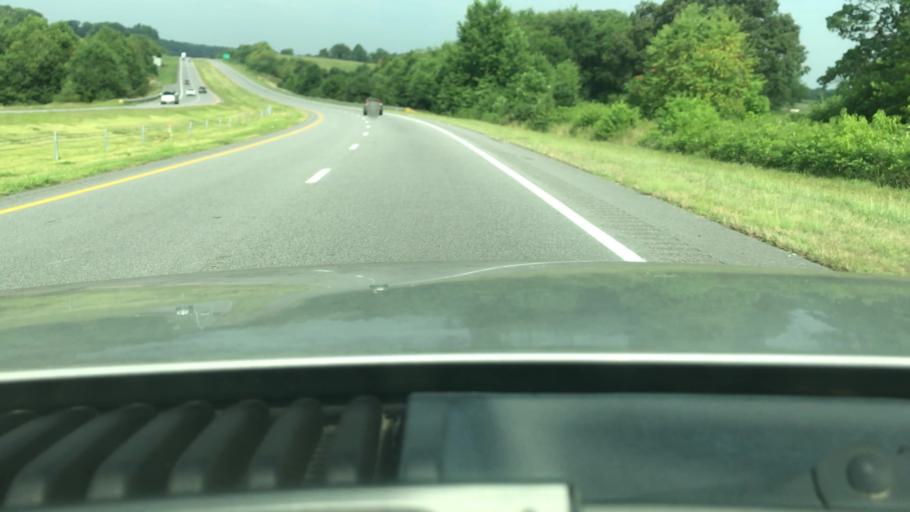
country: US
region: North Carolina
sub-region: Yadkin County
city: Jonesville
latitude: 36.1614
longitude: -80.9466
